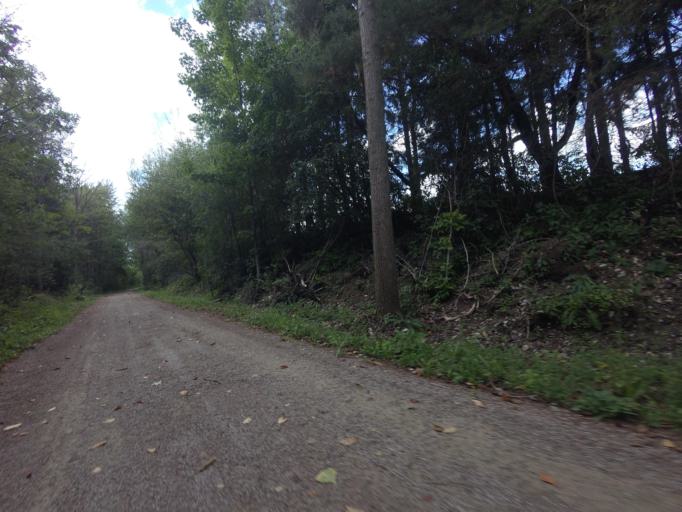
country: CA
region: Ontario
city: Huron East
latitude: 43.7244
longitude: -81.4071
